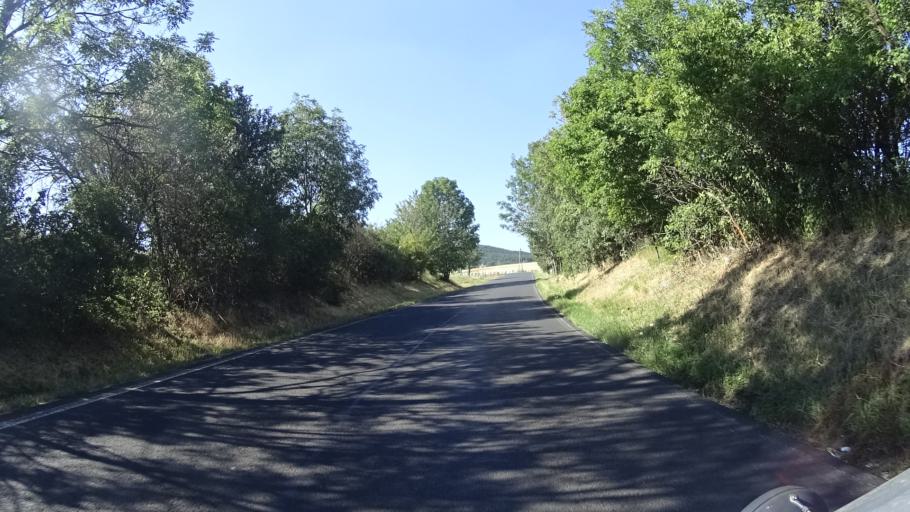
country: CZ
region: Ustecky
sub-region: Okres Litomerice
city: Litomerice
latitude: 50.5545
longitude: 14.1247
